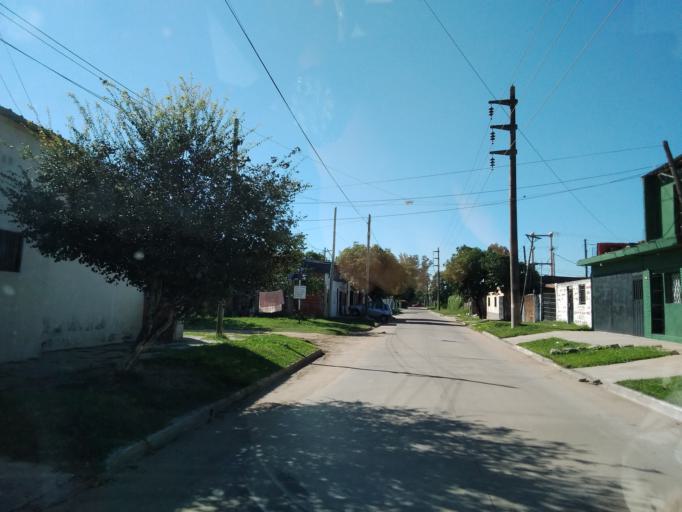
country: AR
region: Corrientes
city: Corrientes
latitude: -27.4691
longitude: -58.7923
